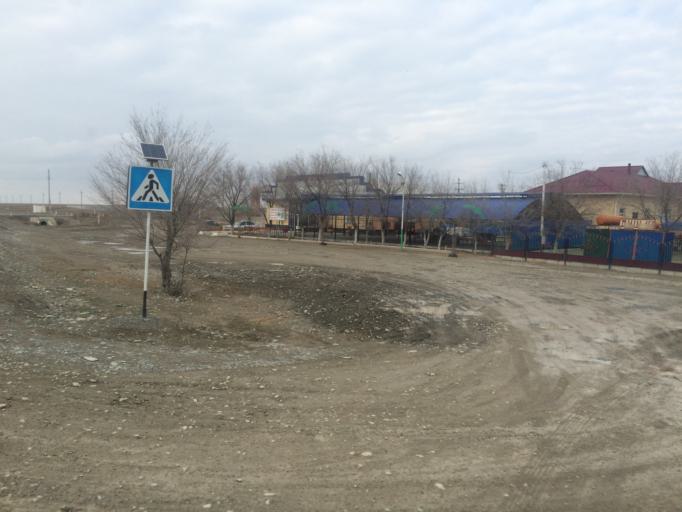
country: KZ
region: Qyzylorda
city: Shalqiya
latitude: 43.6056
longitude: 67.6721
